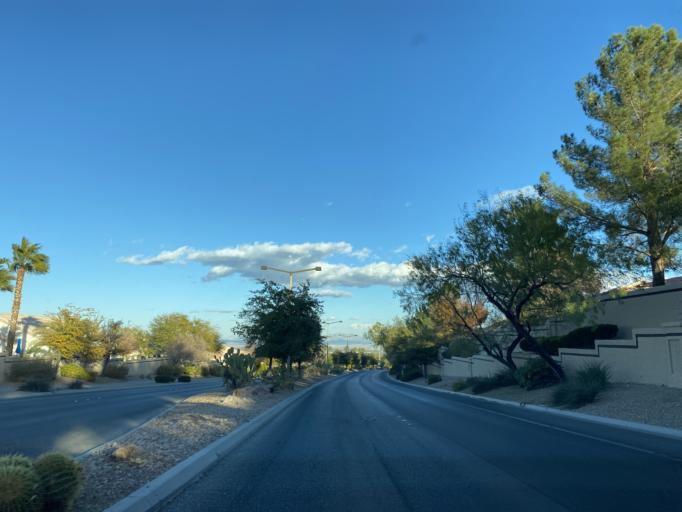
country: US
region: Nevada
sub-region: Clark County
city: Summerlin South
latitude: 36.2050
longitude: -115.3248
